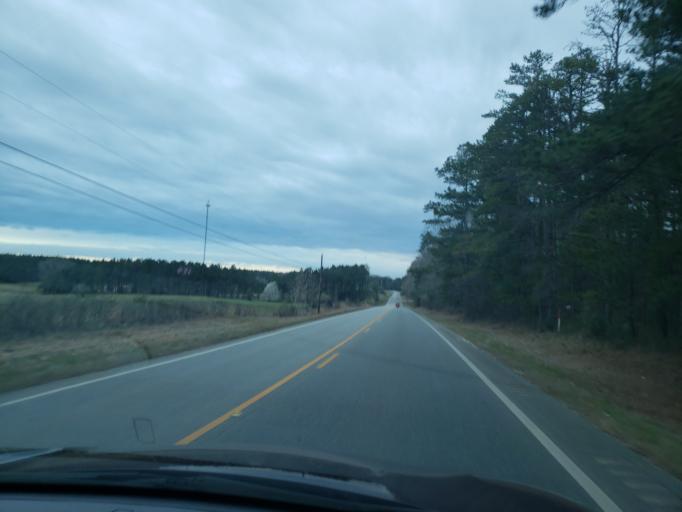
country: US
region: Alabama
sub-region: Chambers County
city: Lafayette
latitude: 32.9267
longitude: -85.3956
